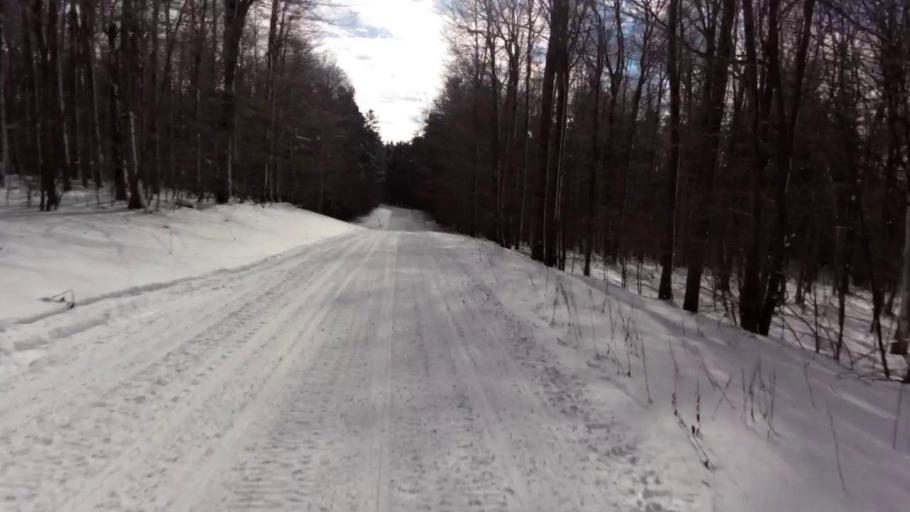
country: US
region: Pennsylvania
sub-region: McKean County
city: Bradford
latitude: 42.0299
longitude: -78.7132
